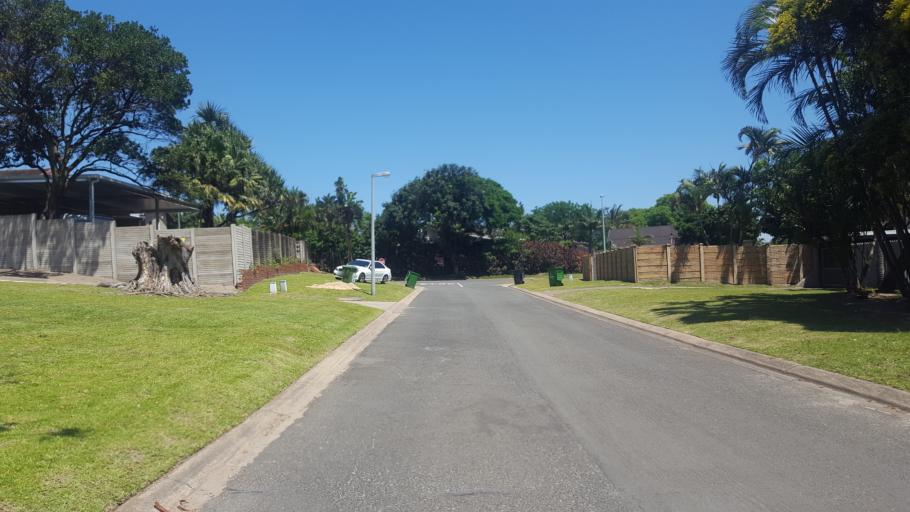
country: ZA
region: KwaZulu-Natal
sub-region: uThungulu District Municipality
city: Richards Bay
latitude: -28.7627
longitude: 32.0644
